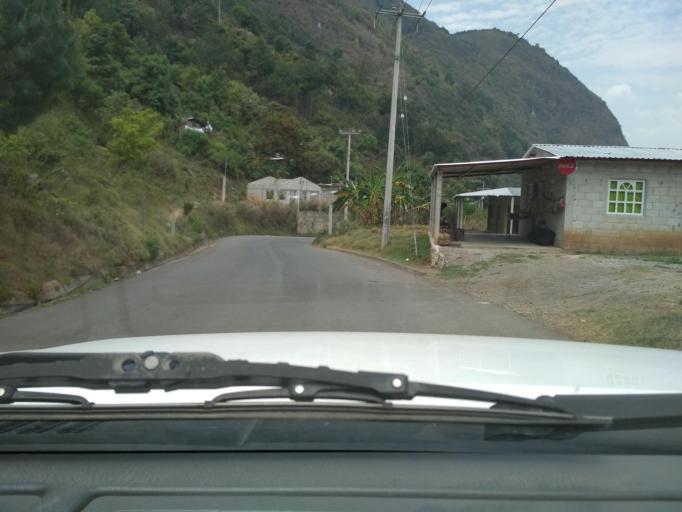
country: MX
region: Veracruz
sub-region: Camerino Z. Mendoza
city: La Cuesta
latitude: 18.7882
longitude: -97.1664
